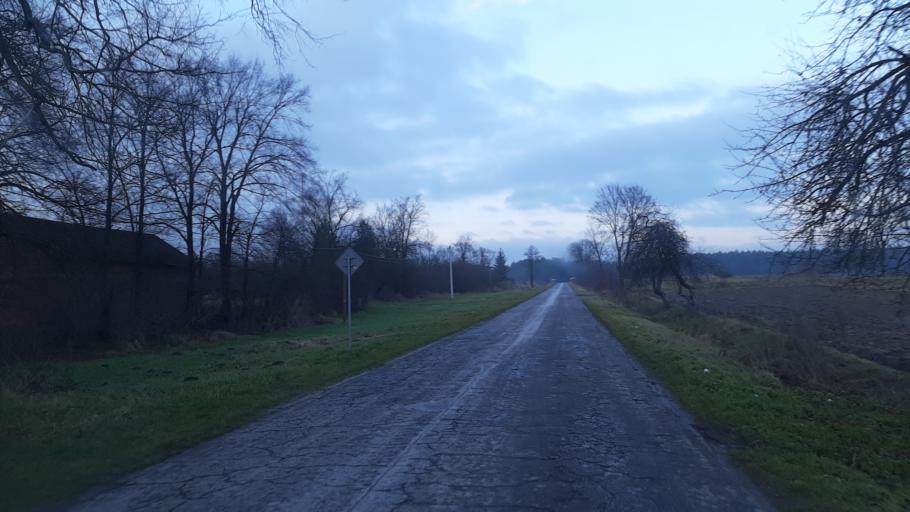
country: PL
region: Lublin Voivodeship
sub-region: Powiat lubartowski
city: Kamionka
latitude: 51.4745
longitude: 22.4664
